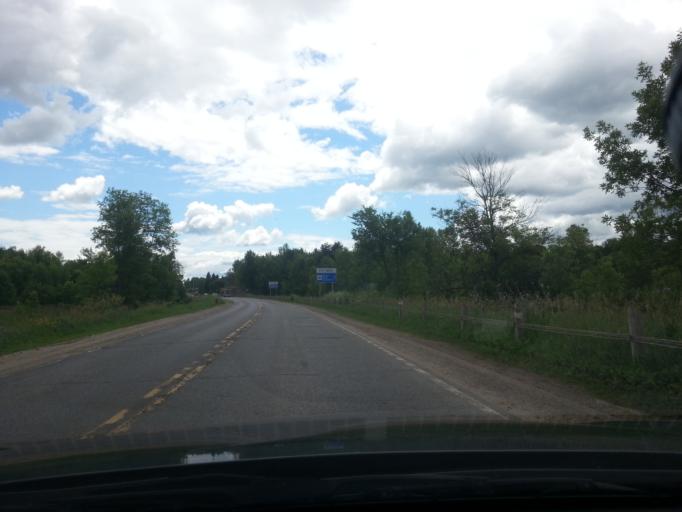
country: CA
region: Ontario
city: Gananoque
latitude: 44.6085
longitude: -76.2274
